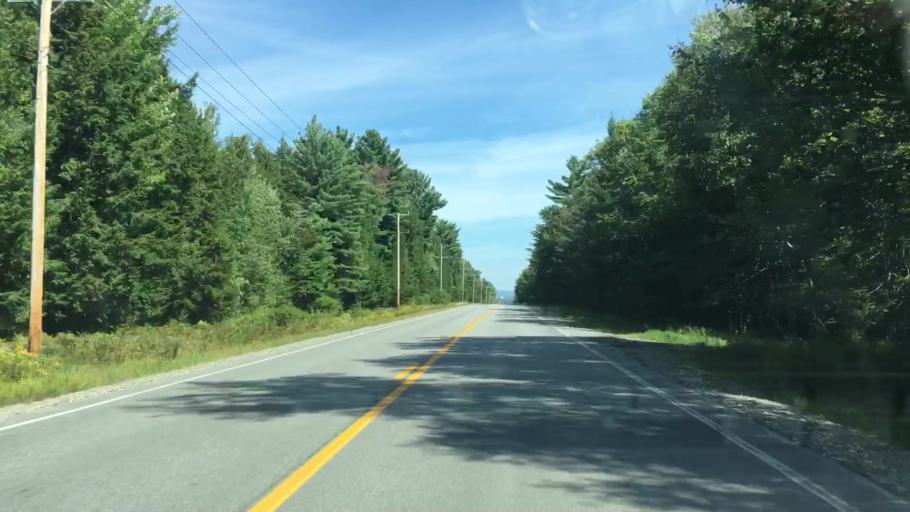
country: US
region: Maine
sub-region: Penobscot County
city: Howland
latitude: 45.2318
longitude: -68.7628
